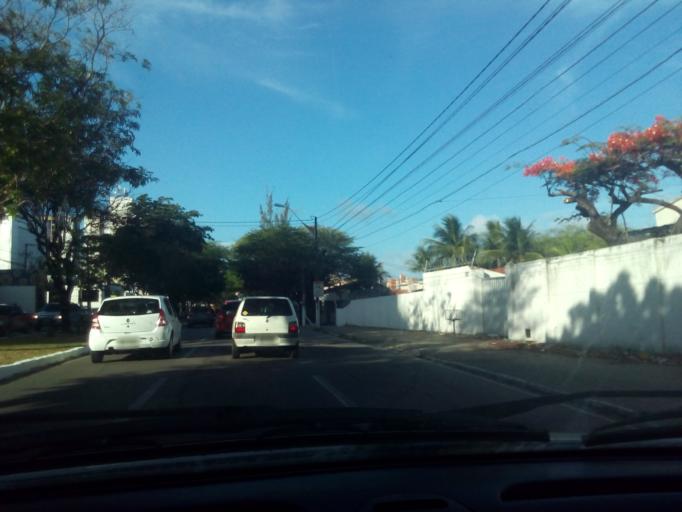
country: BR
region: Rio Grande do Norte
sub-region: Natal
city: Natal
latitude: -5.8069
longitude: -35.2029
